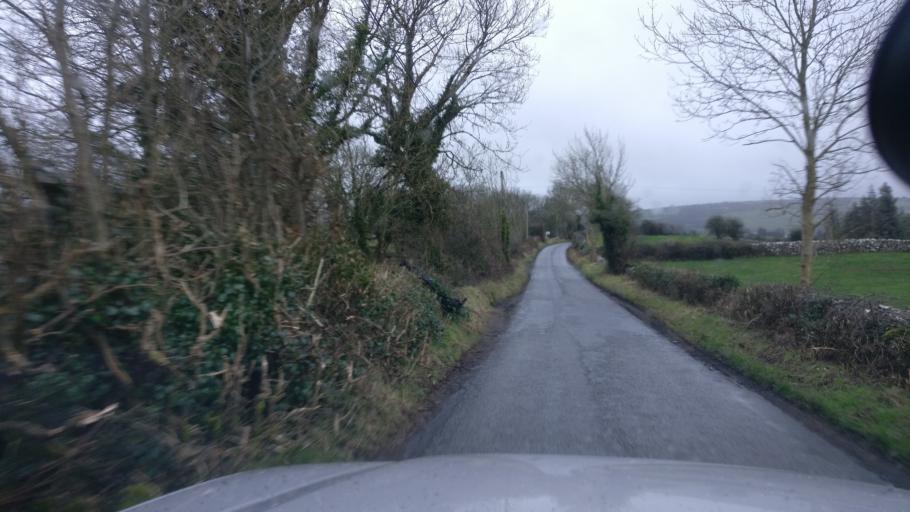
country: IE
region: Connaught
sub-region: County Galway
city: Loughrea
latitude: 53.1877
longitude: -8.6603
